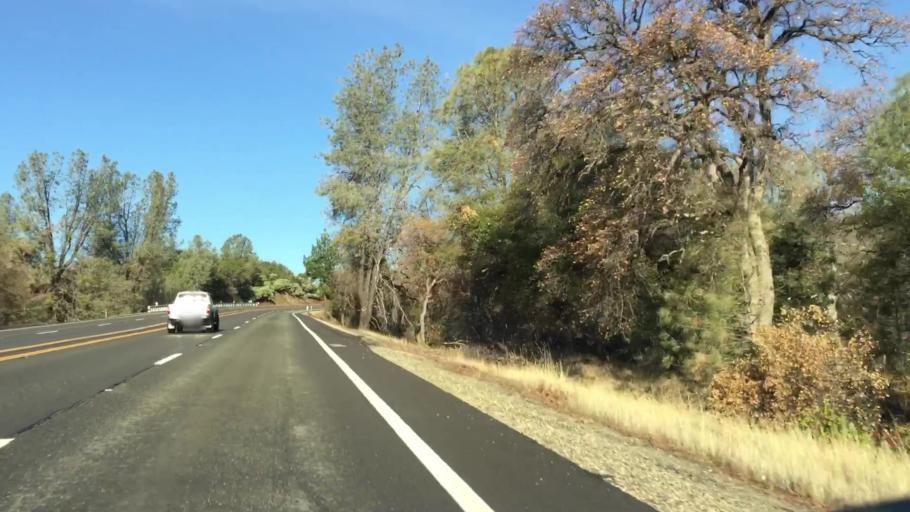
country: US
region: California
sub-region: Butte County
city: Paradise
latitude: 39.6783
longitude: -121.5450
